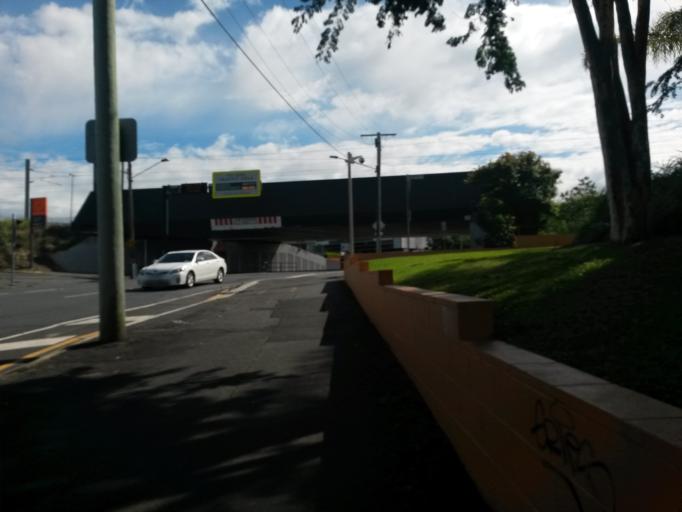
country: AU
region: Queensland
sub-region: Brisbane
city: Woolloongabba
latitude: -27.4967
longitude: 153.0416
